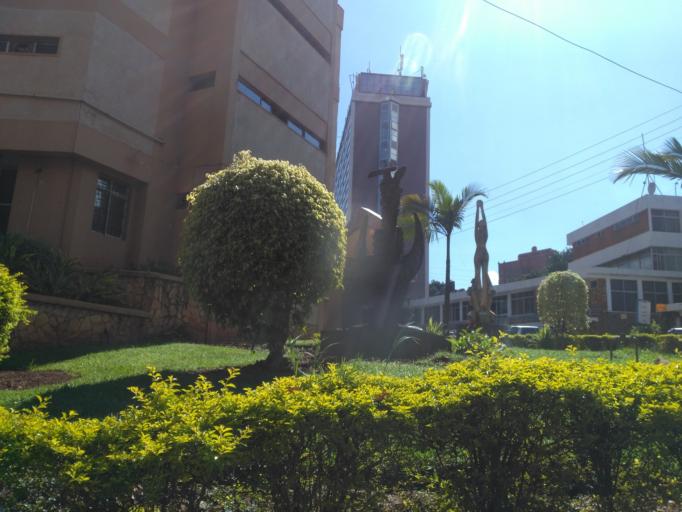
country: UG
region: Central Region
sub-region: Kampala District
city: Kampala
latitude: 0.3201
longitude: 32.5887
